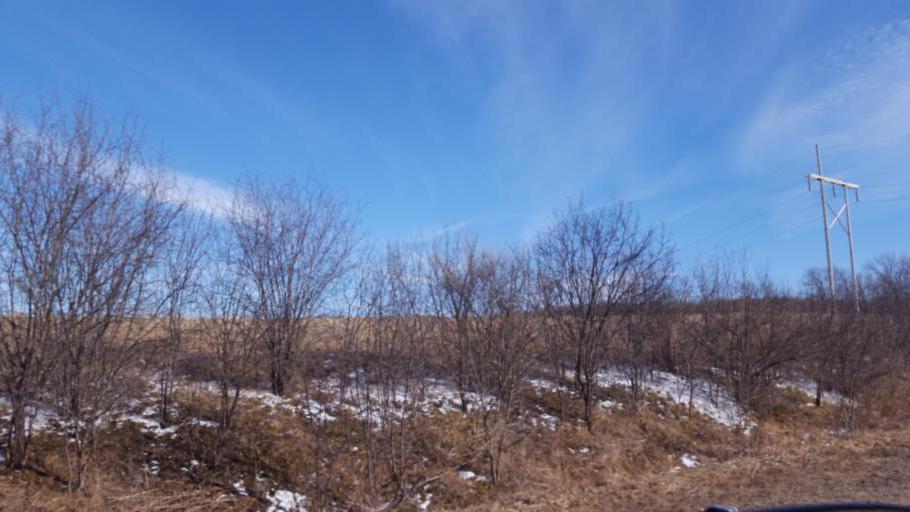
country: US
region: New York
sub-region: Allegany County
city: Wellsville
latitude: 42.1172
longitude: -77.9954
